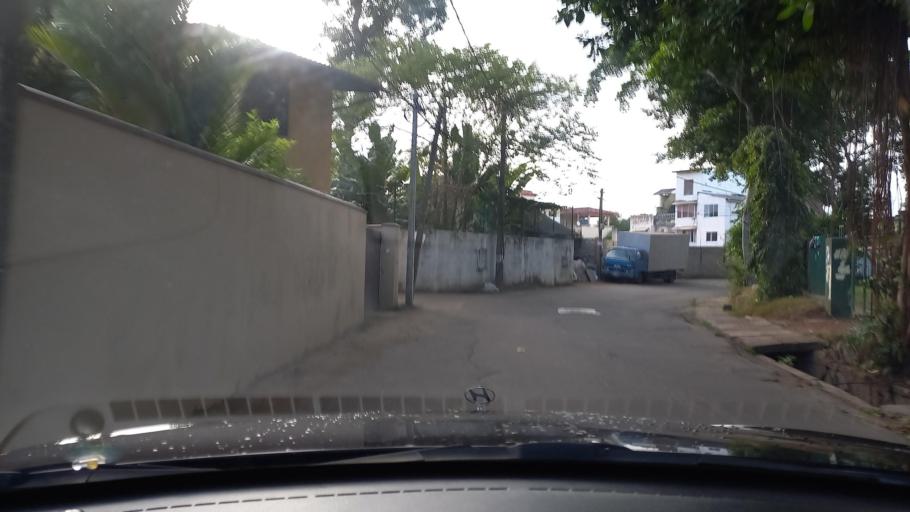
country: LK
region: Western
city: Pita Kotte
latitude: 6.8766
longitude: 79.8843
